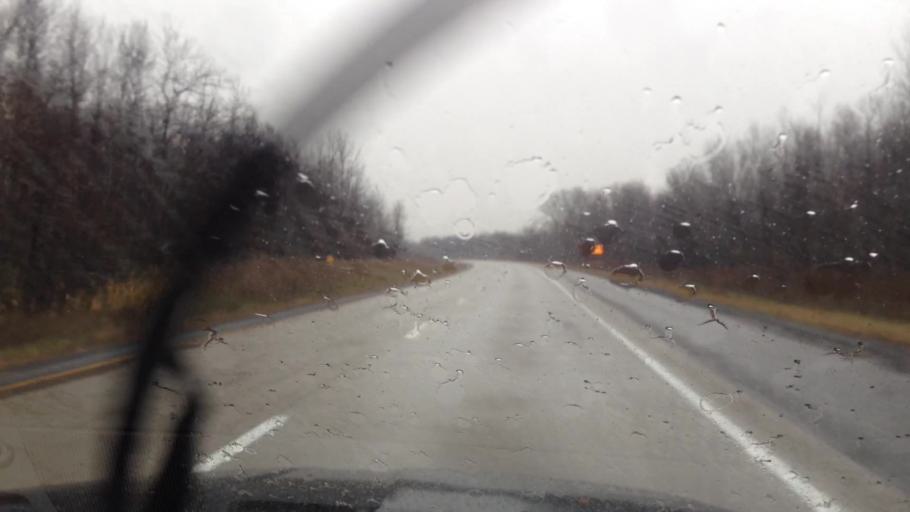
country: CA
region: Ontario
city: Hawkesbury
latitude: 45.4482
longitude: -74.7133
